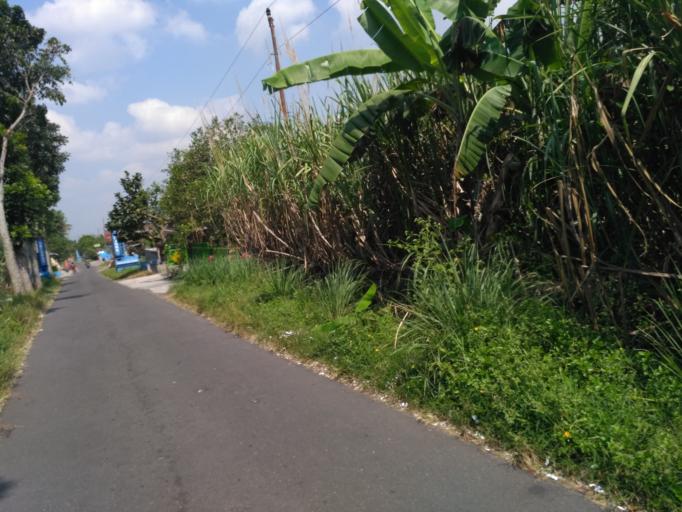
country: ID
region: Daerah Istimewa Yogyakarta
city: Depok
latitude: -7.7124
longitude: 110.4239
